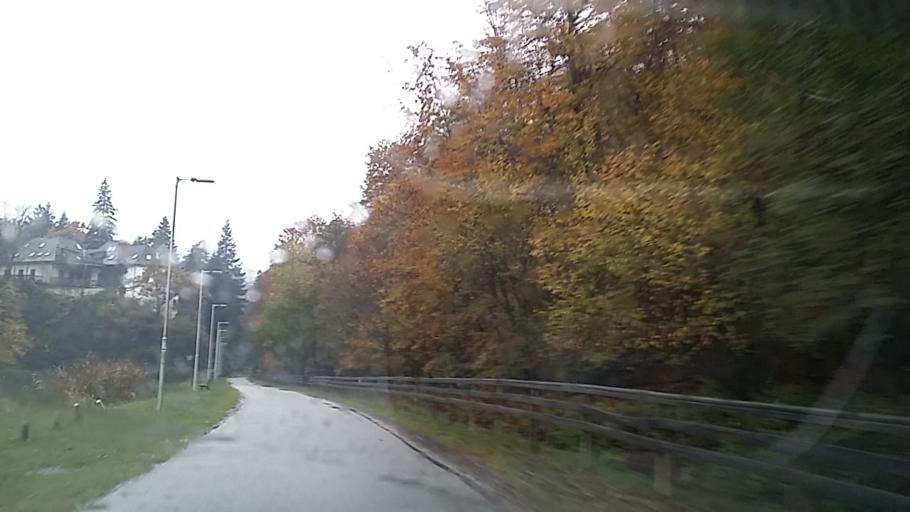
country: HU
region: Borsod-Abauj-Zemplen
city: Tolcsva
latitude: 48.4282
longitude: 21.4423
